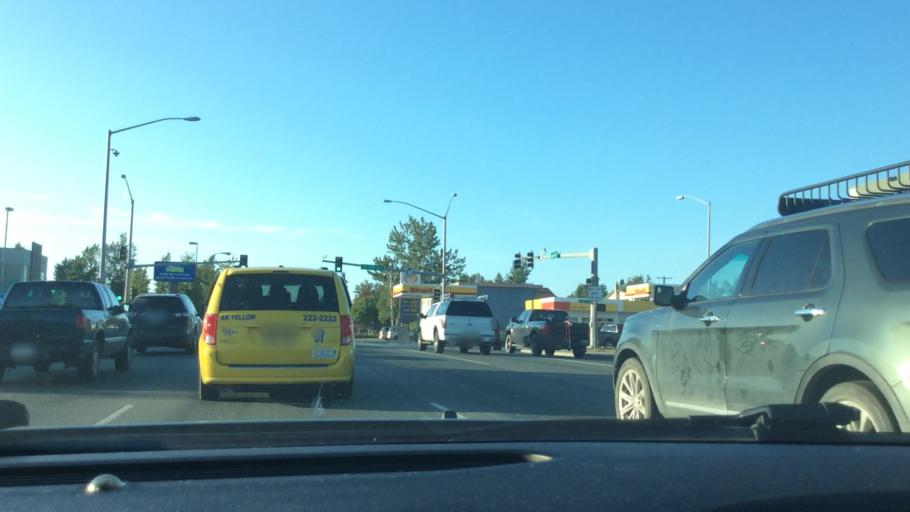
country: US
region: Alaska
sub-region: Anchorage Municipality
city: Anchorage
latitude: 61.2072
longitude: -149.8670
